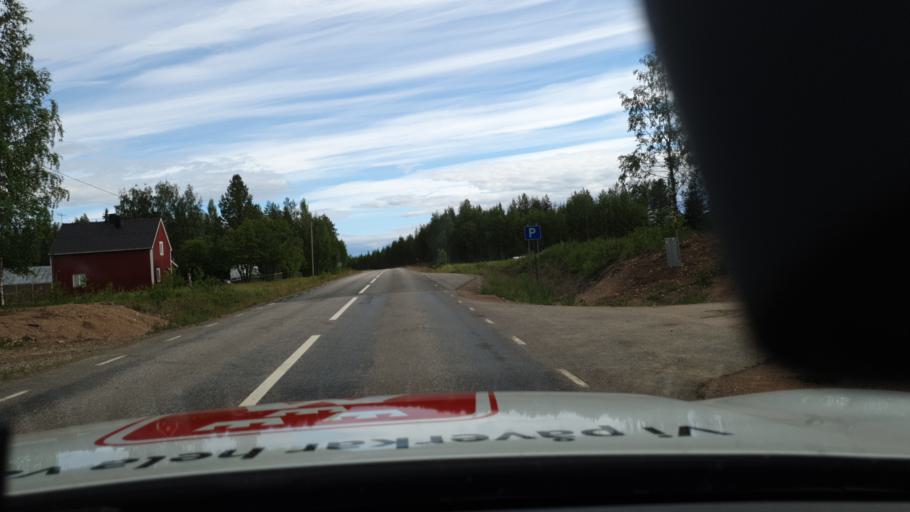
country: SE
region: Norrbotten
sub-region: Overkalix Kommun
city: OEverkalix
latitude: 66.5315
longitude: 22.7571
